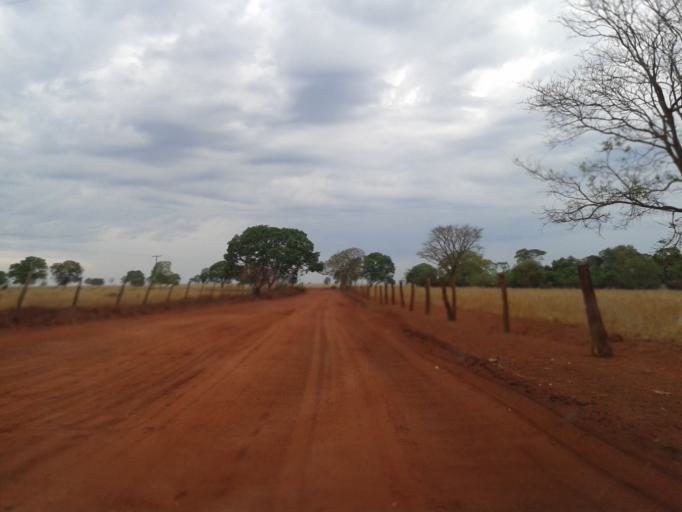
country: BR
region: Minas Gerais
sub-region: Ituiutaba
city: Ituiutaba
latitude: -18.9297
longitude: -49.7411
